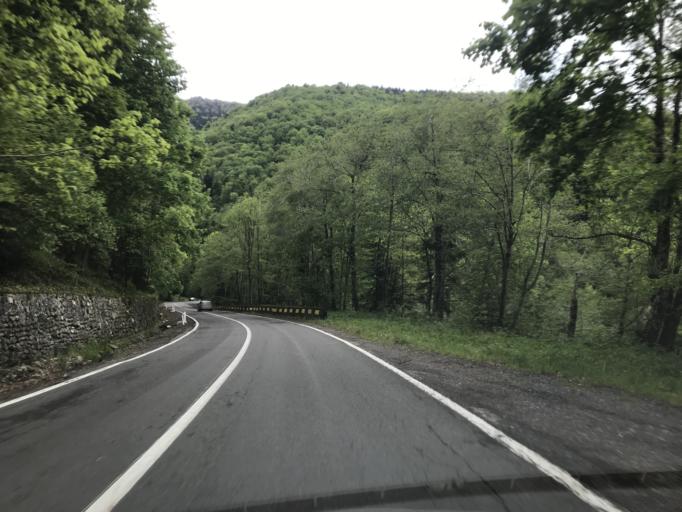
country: RO
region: Sibiu
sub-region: Comuna Cartisoara
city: Cartisoara
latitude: 45.6697
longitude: 24.5781
